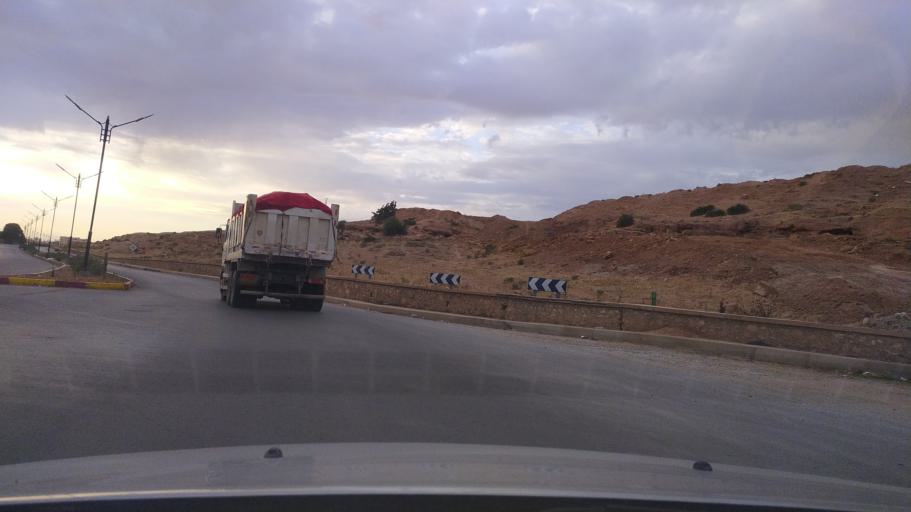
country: DZ
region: Tiaret
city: Frenda
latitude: 35.0510
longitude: 1.0740
